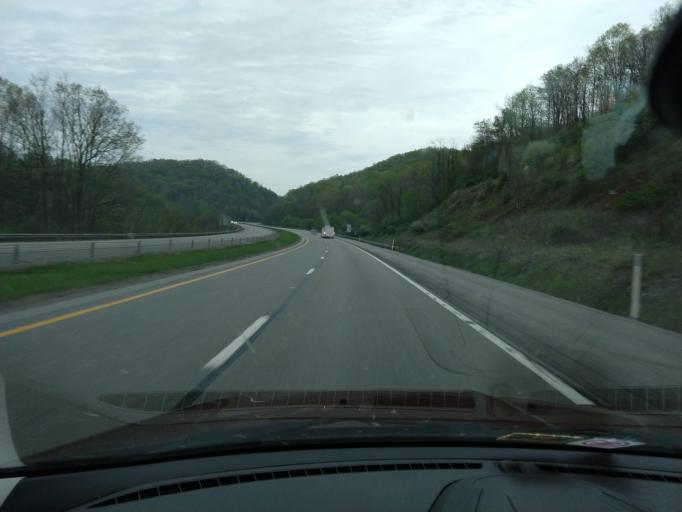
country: US
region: West Virginia
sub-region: Lewis County
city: Weston
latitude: 38.9718
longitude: -80.5116
